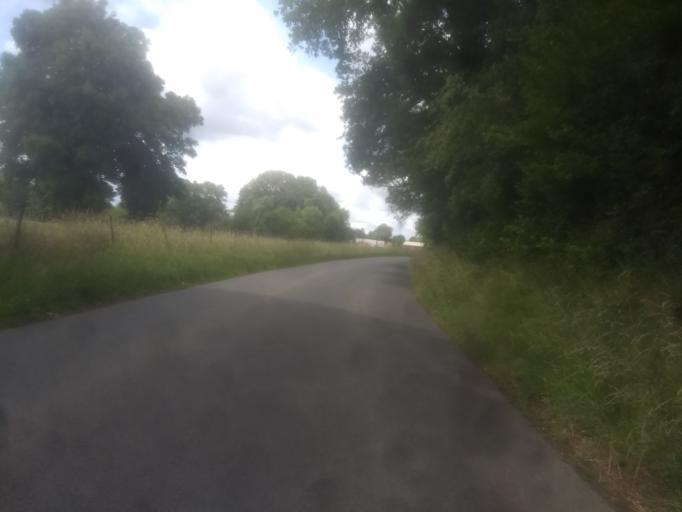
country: FR
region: Nord-Pas-de-Calais
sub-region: Departement du Pas-de-Calais
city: Mont-Saint-Eloi
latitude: 50.3413
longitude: 2.6874
